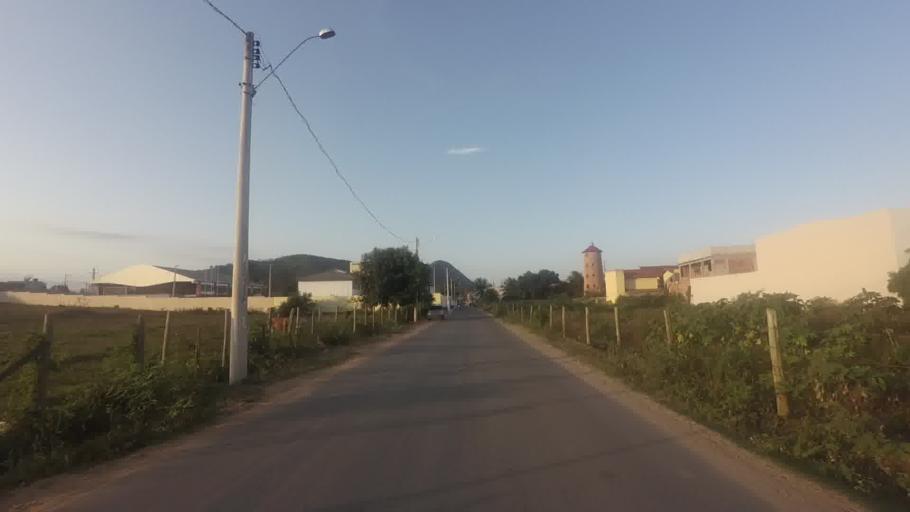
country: BR
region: Espirito Santo
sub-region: Piuma
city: Piuma
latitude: -20.8921
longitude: -40.7830
